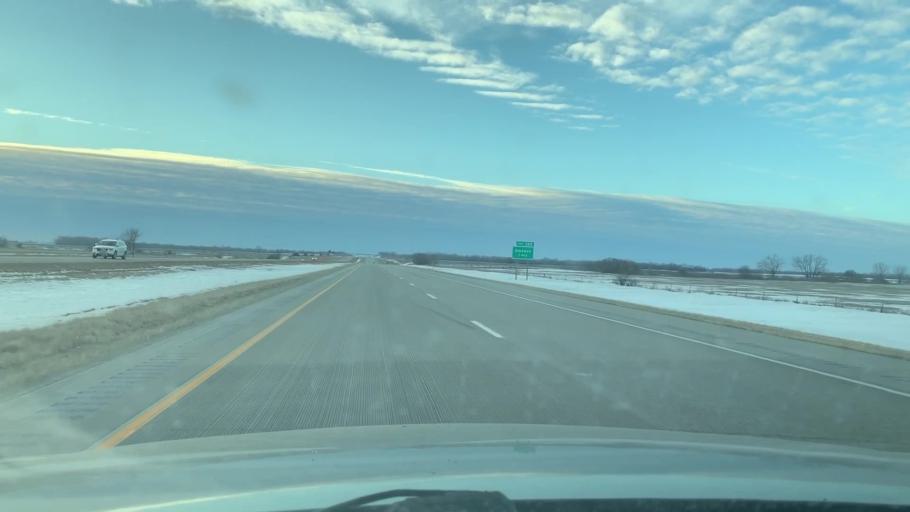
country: US
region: North Dakota
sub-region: Cass County
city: Casselton
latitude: 46.8761
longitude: -97.4008
